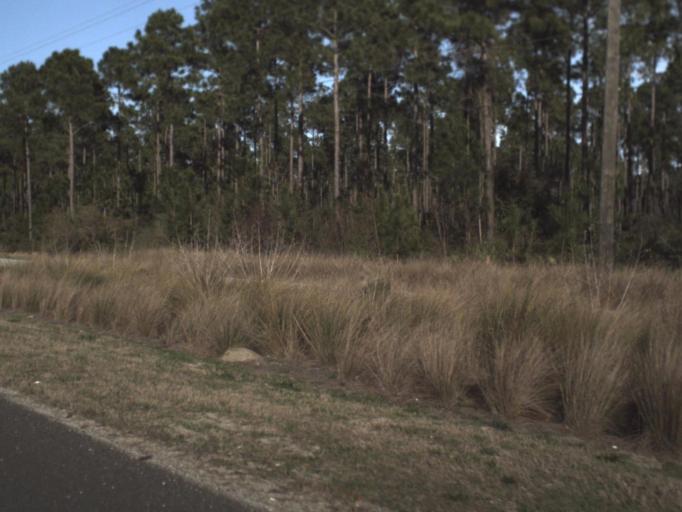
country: US
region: Florida
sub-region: Bay County
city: Laguna Beach
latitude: 30.2427
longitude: -85.8822
